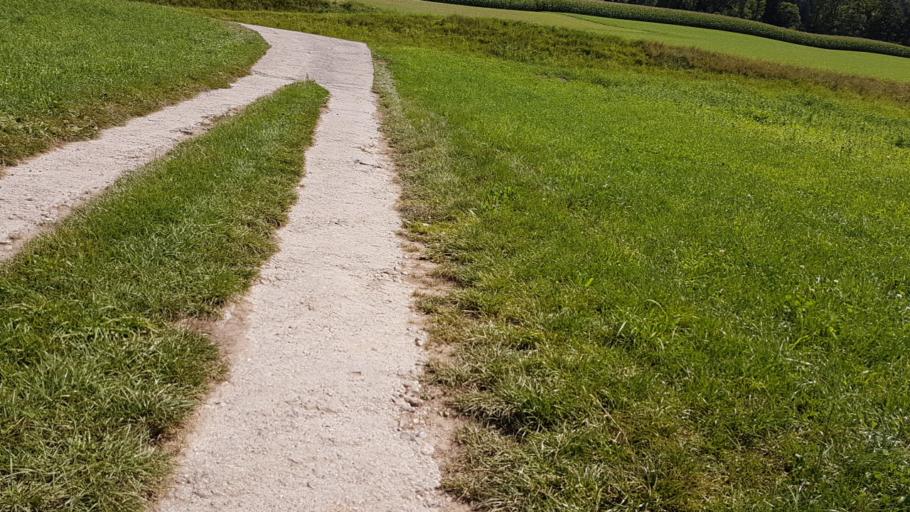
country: CH
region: Bern
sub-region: Bern-Mittelland District
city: Konolfingen
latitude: 46.8629
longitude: 7.6273
